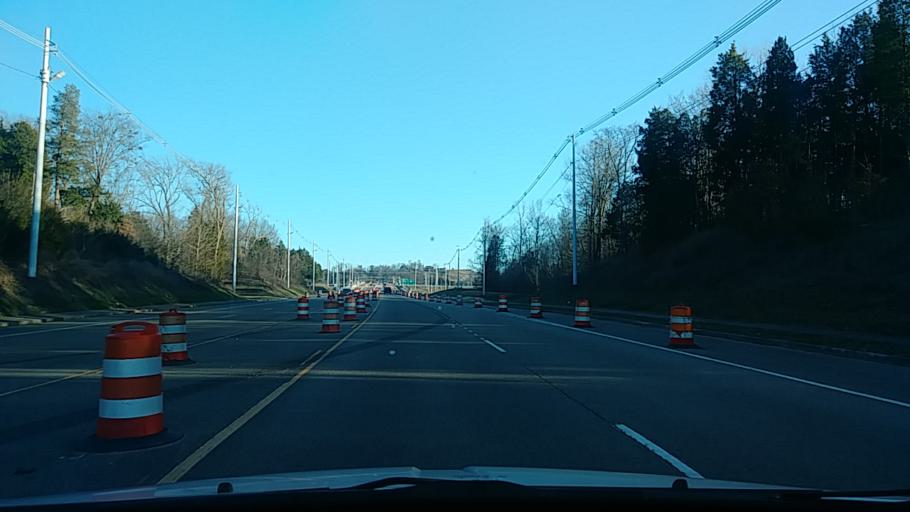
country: US
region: Tennessee
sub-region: Hamblen County
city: Morristown
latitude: 36.1804
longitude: -83.3518
